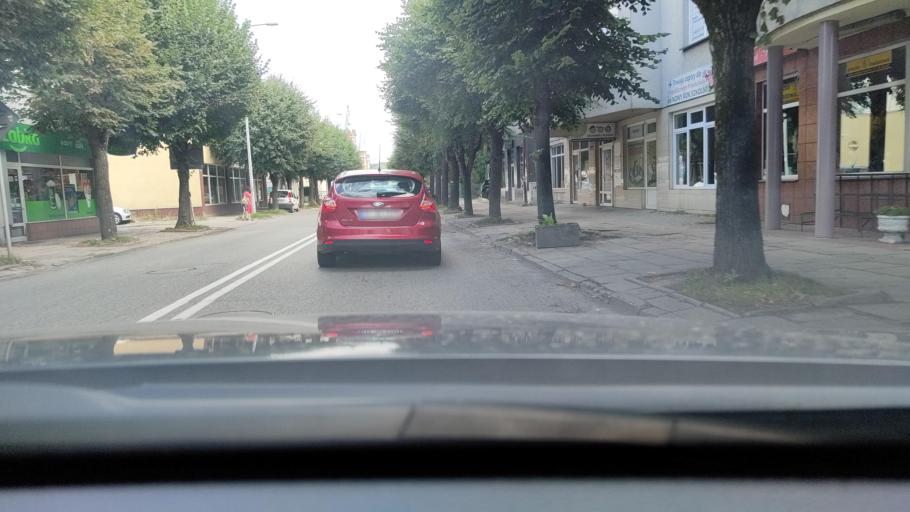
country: PL
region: Pomeranian Voivodeship
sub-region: Powiat wejherowski
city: Wejherowo
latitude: 54.5995
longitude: 18.2326
